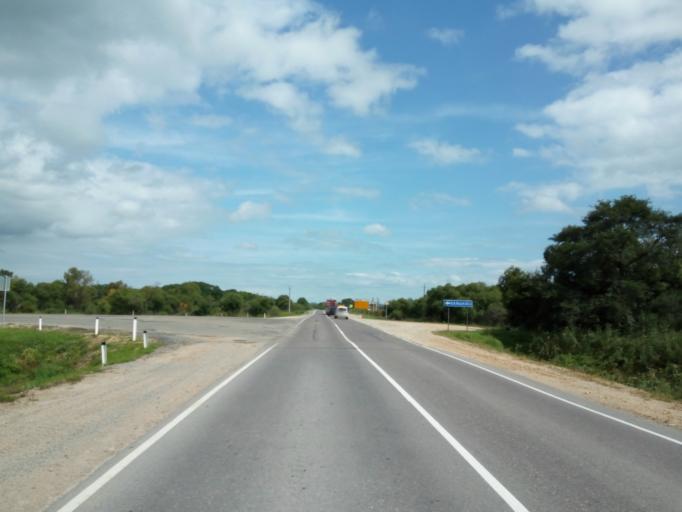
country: RU
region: Primorskiy
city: Dal'nerechensk
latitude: 45.9705
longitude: 133.7861
